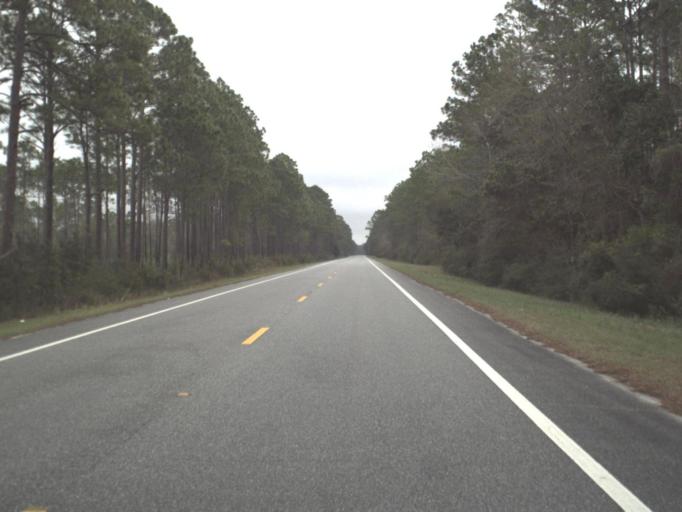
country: US
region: Florida
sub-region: Franklin County
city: Eastpoint
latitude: 29.8293
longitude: -84.8844
